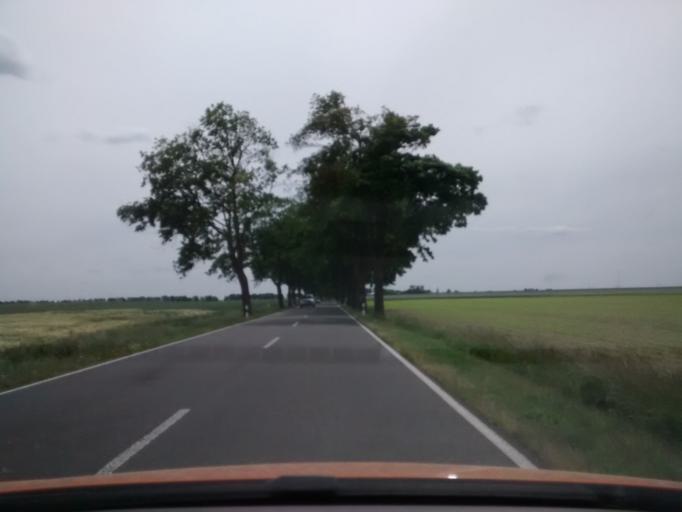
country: DE
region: Brandenburg
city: Juterbog
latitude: 51.9183
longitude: 13.1300
